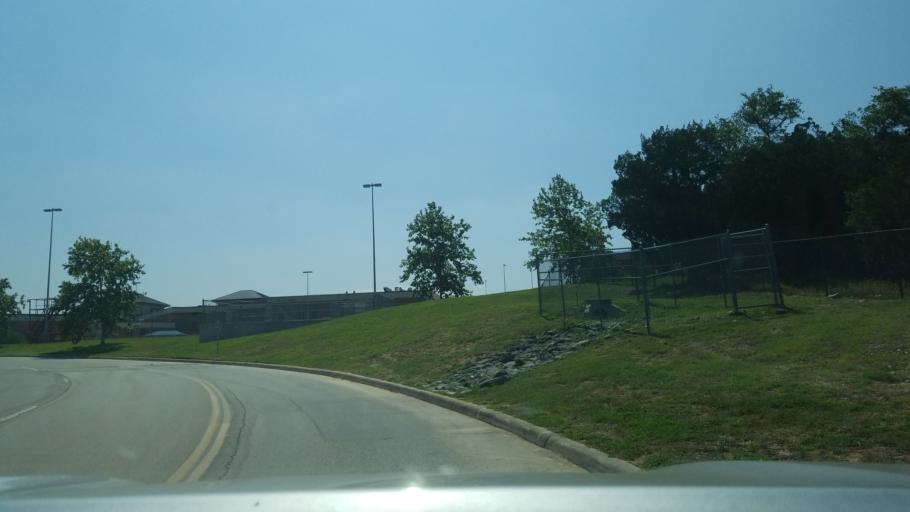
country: US
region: Texas
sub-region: Bexar County
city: Timberwood Park
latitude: 29.6577
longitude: -98.4378
